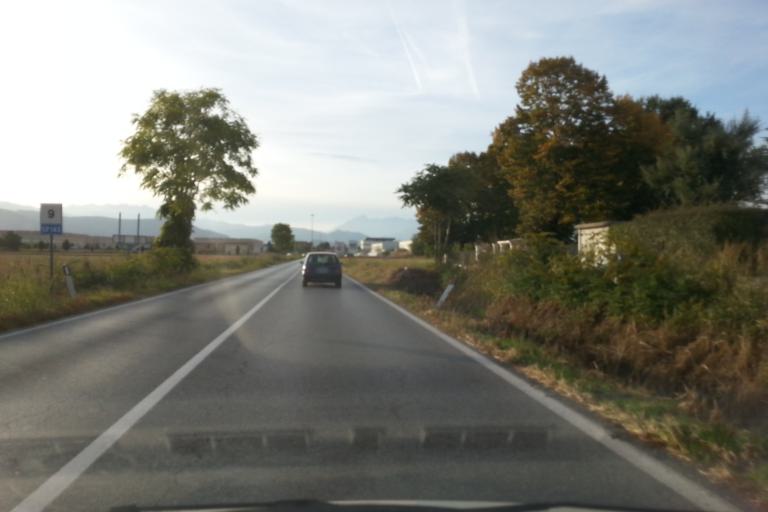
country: IT
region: Piedmont
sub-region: Provincia di Torino
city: Pasta
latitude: 44.9964
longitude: 7.5586
